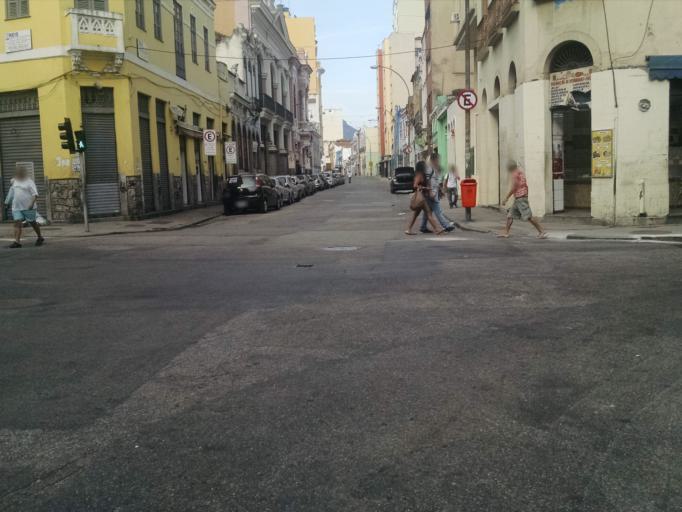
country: BR
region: Rio de Janeiro
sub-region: Rio De Janeiro
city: Rio de Janeiro
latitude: -22.9103
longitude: -43.1882
